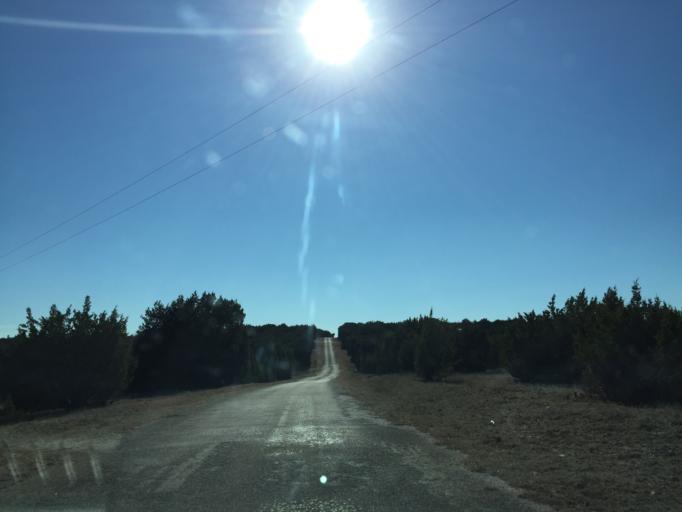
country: US
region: Texas
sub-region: Lampasas County
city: Lampasas
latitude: 30.9428
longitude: -98.1657
